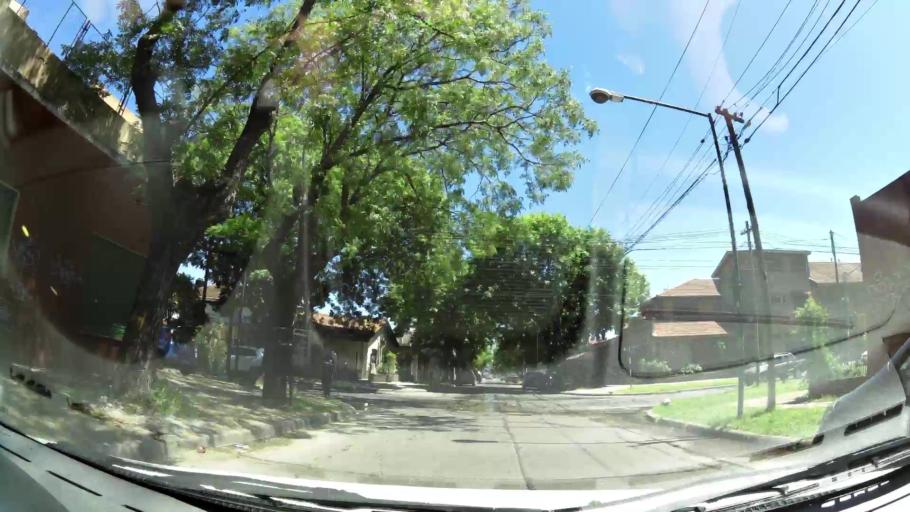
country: AR
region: Buenos Aires
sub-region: Partido de General San Martin
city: General San Martin
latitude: -34.5173
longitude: -58.5446
